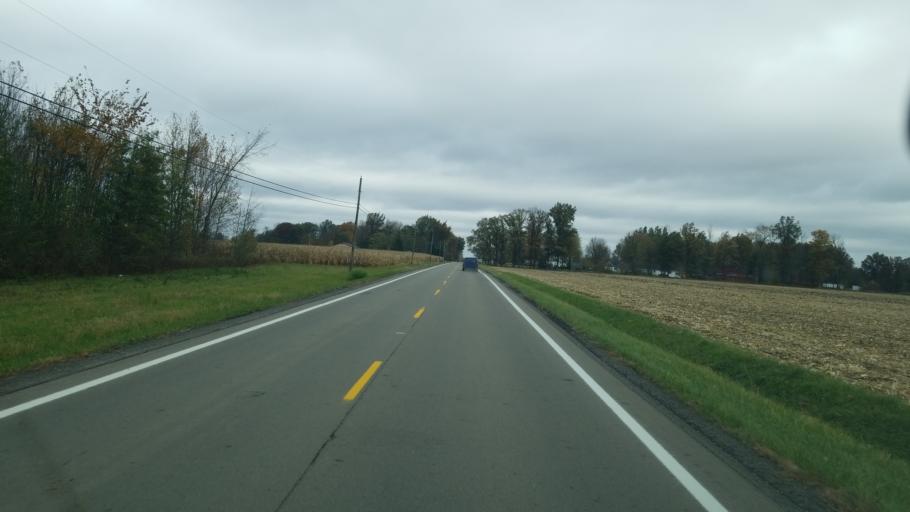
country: US
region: Ohio
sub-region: Crawford County
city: Galion
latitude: 40.8041
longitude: -82.8566
